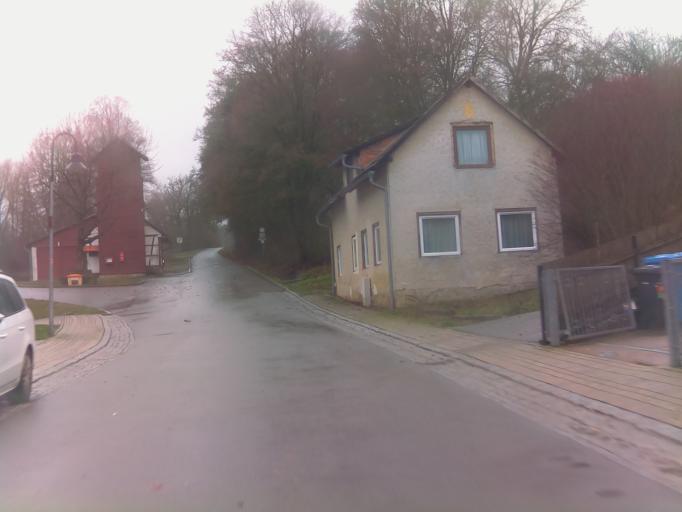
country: DE
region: Thuringia
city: Dingsleben
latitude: 50.4314
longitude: 10.5919
